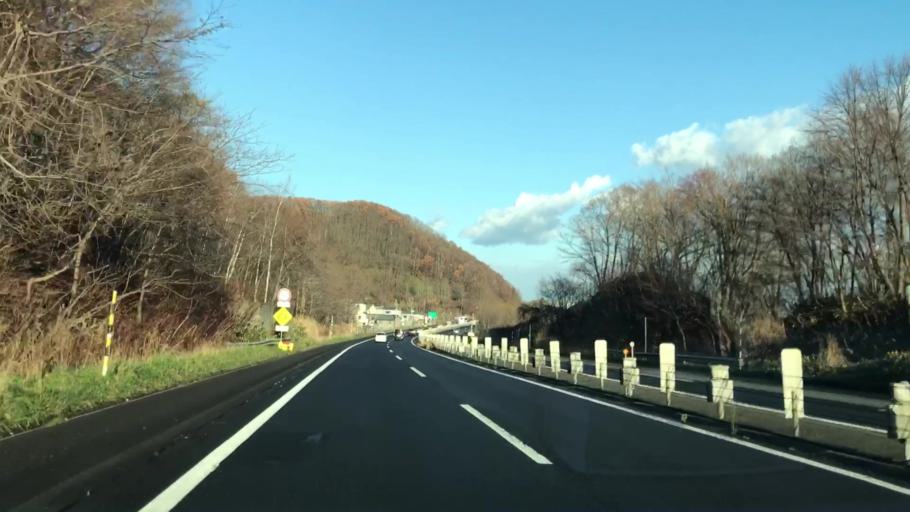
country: JP
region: Hokkaido
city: Sapporo
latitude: 43.1027
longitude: 141.2453
